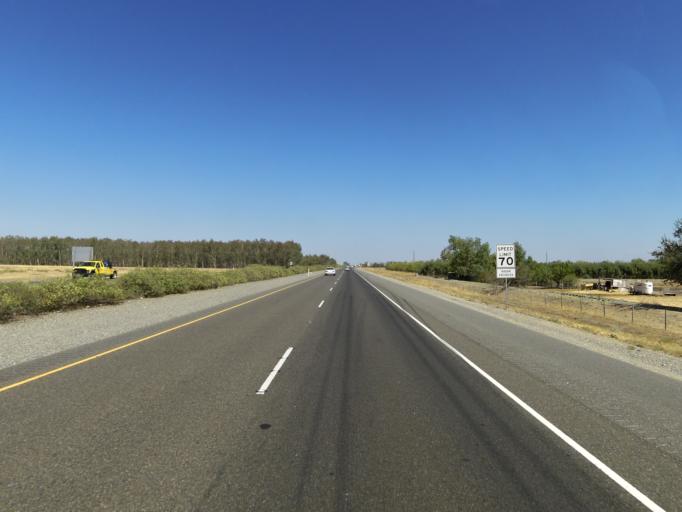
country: US
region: California
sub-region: Glenn County
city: Orland
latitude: 39.7586
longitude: -122.2052
